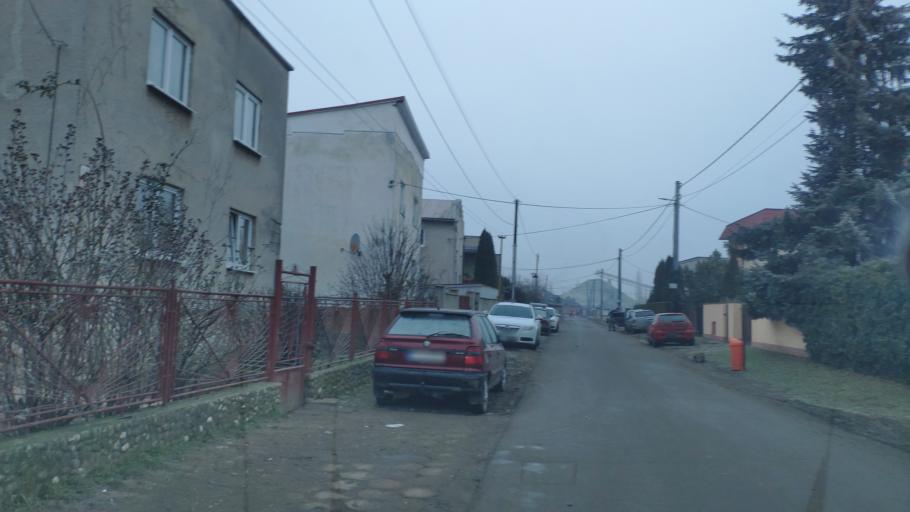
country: SK
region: Kosicky
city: Kosice
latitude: 48.6177
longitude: 21.3190
